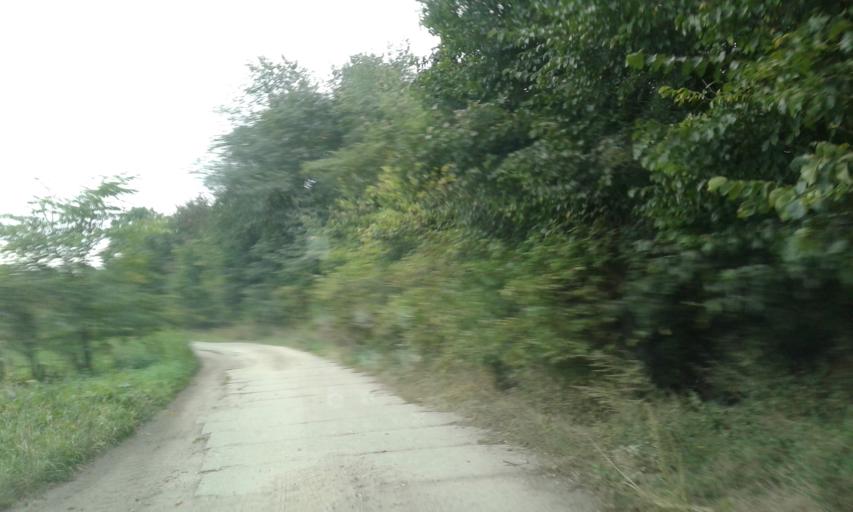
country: PL
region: West Pomeranian Voivodeship
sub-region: Powiat pyrzycki
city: Warnice
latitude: 53.1795
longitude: 14.9980
